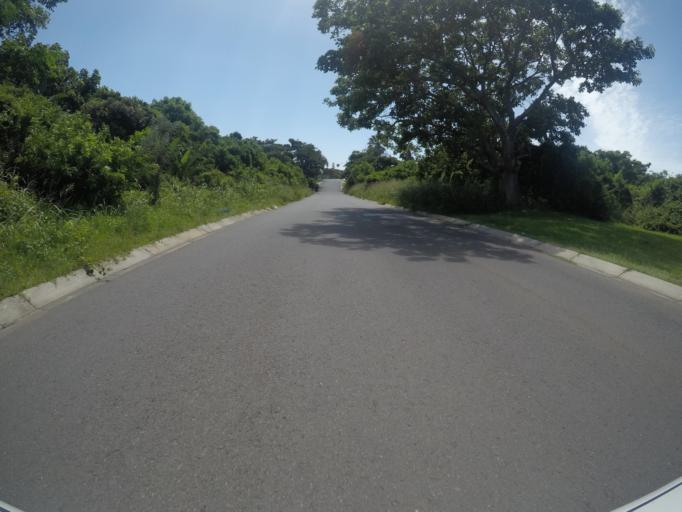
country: ZA
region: Eastern Cape
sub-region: Buffalo City Metropolitan Municipality
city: East London
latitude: -32.9489
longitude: 28.0019
